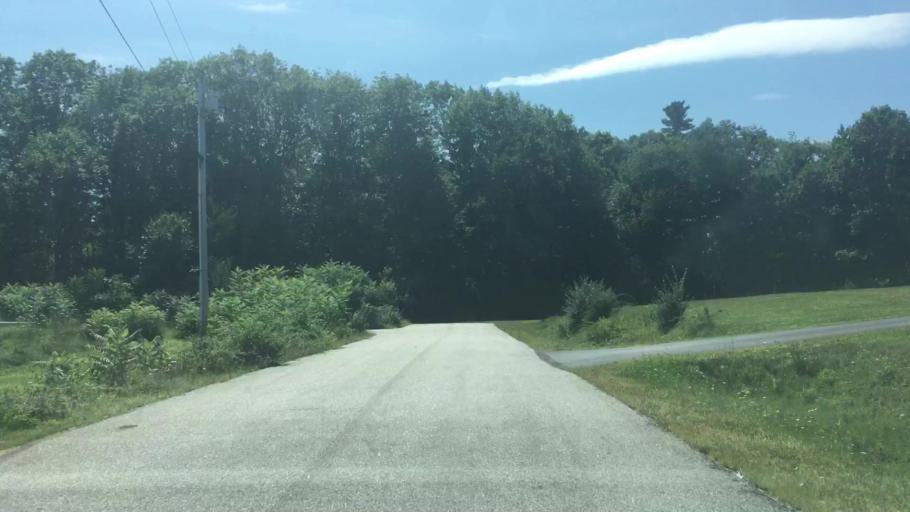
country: US
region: Maine
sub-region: Kennebec County
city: Monmouth
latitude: 44.2052
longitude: -69.9569
